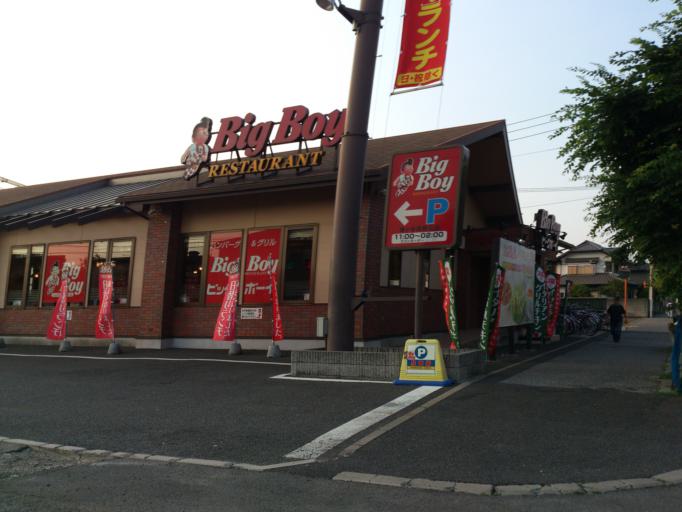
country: JP
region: Chiba
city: Funabashi
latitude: 35.7463
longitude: 139.9977
